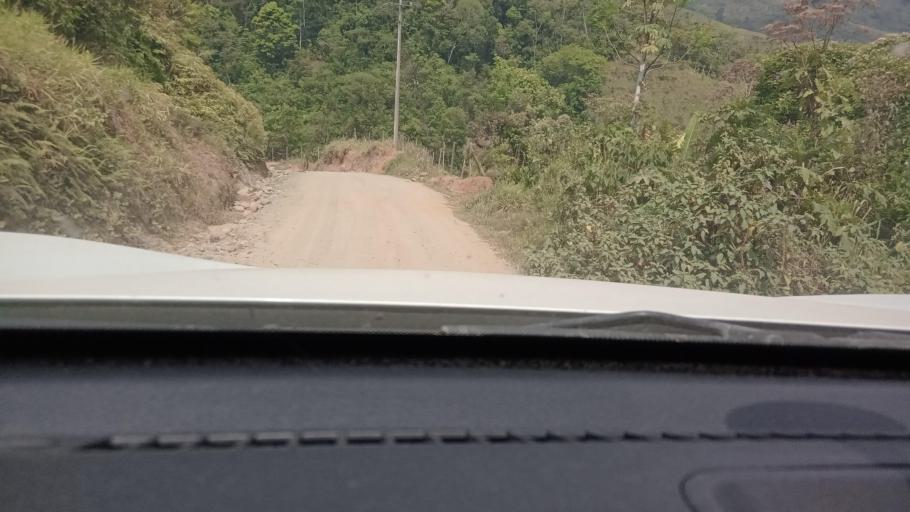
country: MX
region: Tabasco
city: Chontalpa
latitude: 17.4868
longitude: -93.6689
